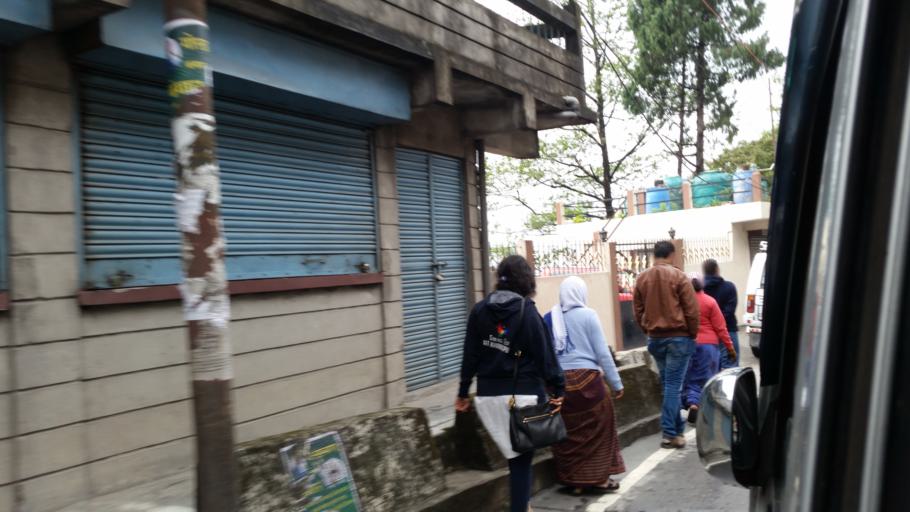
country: IN
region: West Bengal
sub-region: Darjiling
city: Darjiling
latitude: 27.0234
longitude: 88.2540
